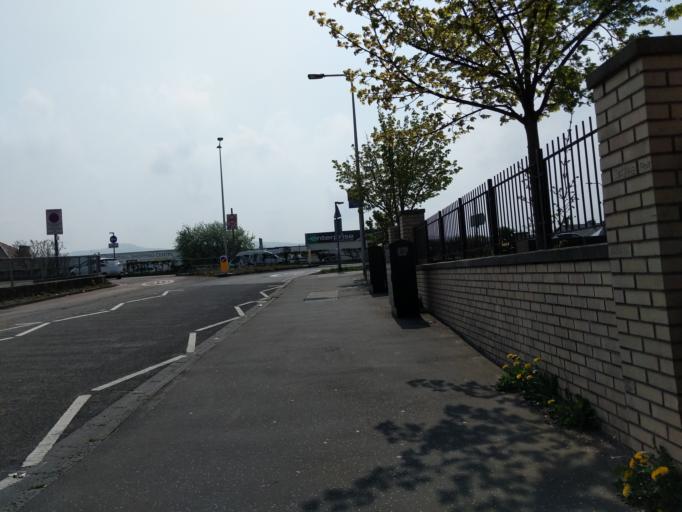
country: GB
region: Scotland
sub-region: Edinburgh
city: Currie
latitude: 55.9234
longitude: -3.2871
